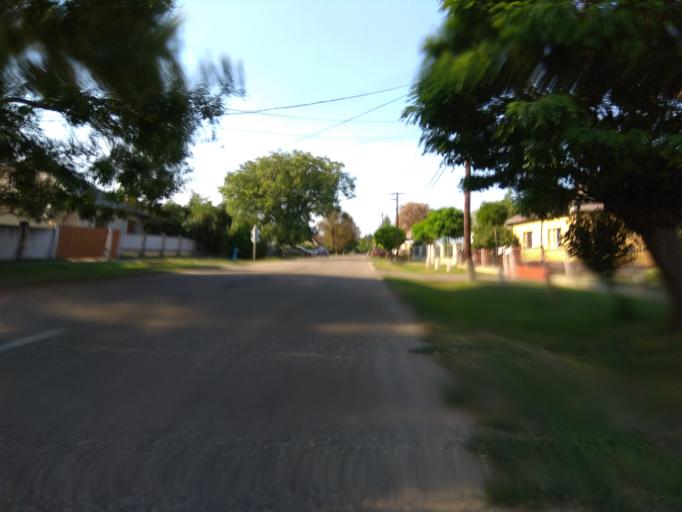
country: HU
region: Borsod-Abauj-Zemplen
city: Onod
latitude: 47.9636
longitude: 20.8838
